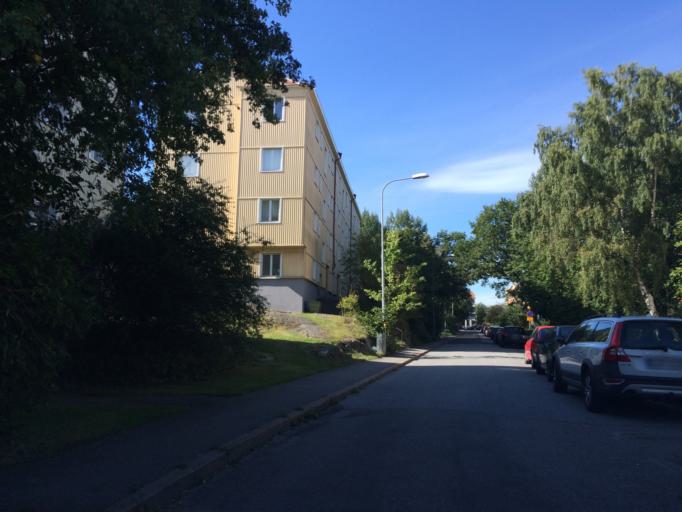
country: SE
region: Stockholm
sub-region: Stockholms Kommun
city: Arsta
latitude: 59.3036
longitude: 17.9970
